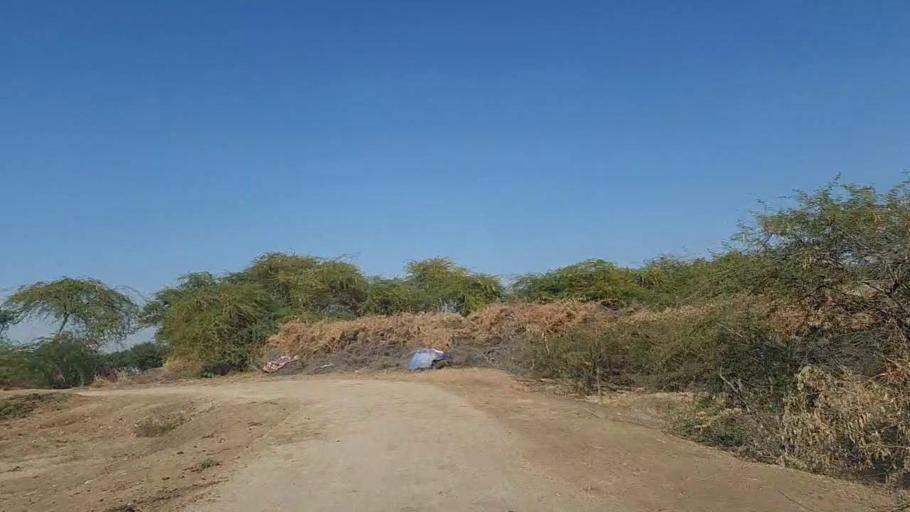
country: PK
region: Sindh
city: Naukot
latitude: 25.0142
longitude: 69.3610
